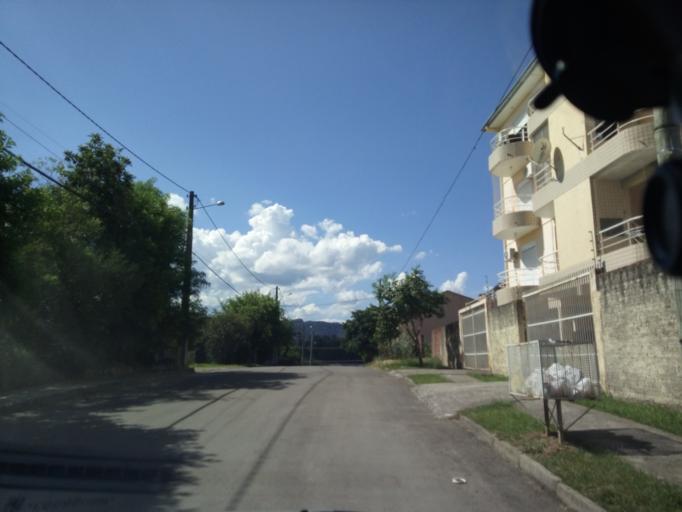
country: BR
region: Rio Grande do Sul
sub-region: Santa Maria
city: Santa Maria
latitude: -29.6979
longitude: -53.7351
